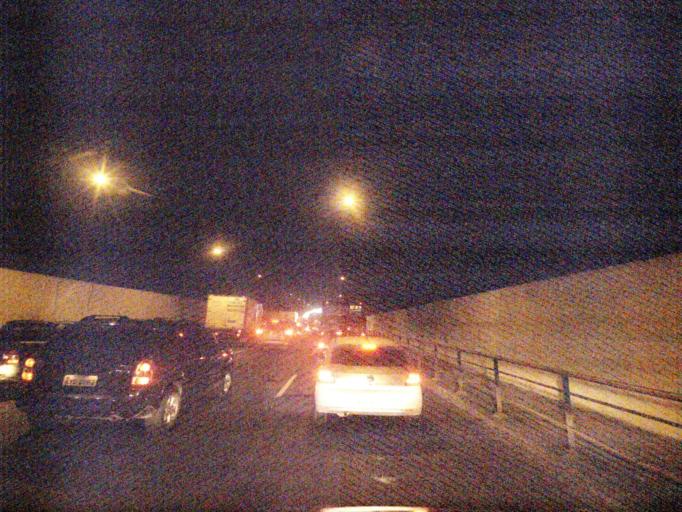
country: BR
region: Rio de Janeiro
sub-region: Niteroi
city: Niteroi
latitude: -22.9105
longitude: -43.0995
